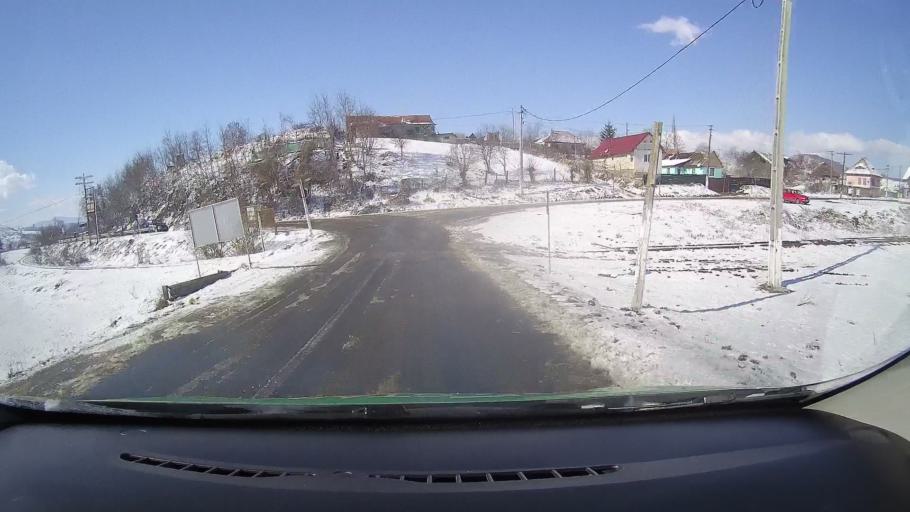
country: RO
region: Sibiu
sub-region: Comuna Rosia
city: Rosia
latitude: 45.8020
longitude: 24.3527
